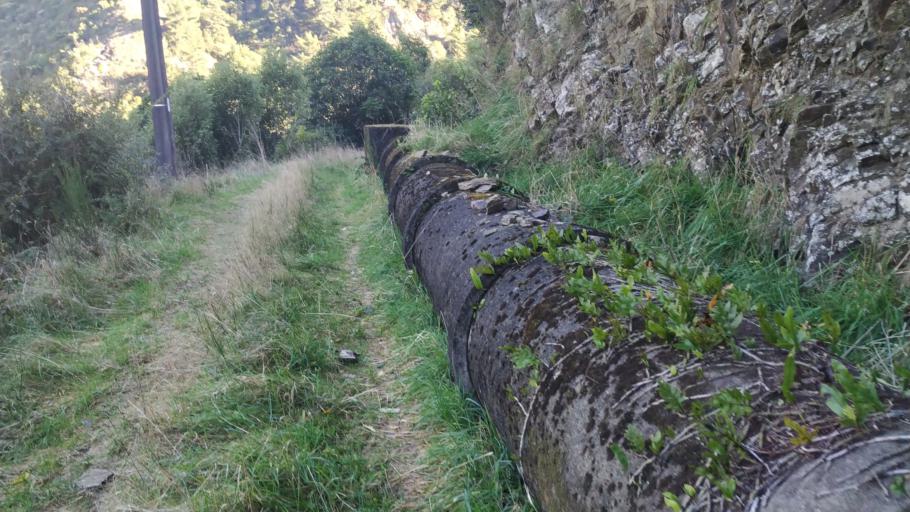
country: NZ
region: Nelson
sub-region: Nelson City
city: Nelson
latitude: -41.2978
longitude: 173.3378
